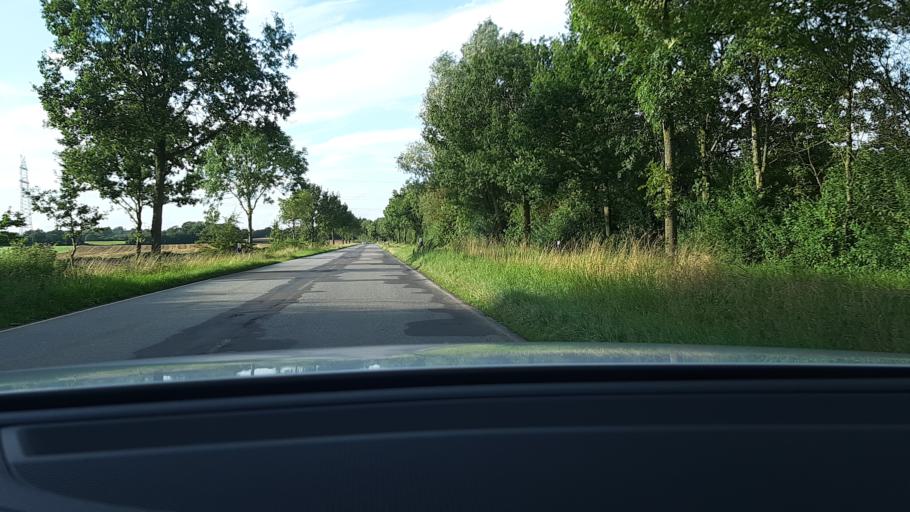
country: DE
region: Schleswig-Holstein
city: Heilshoop
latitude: 53.9013
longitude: 10.5241
